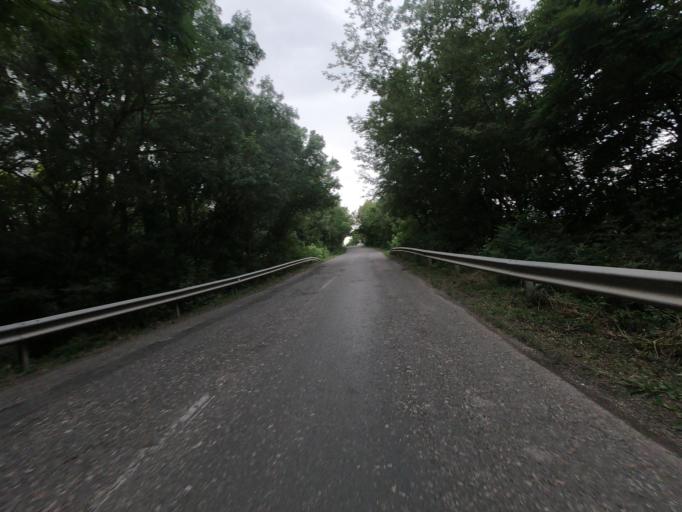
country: HU
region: Heves
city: Poroszlo
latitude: 47.7029
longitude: 20.6390
